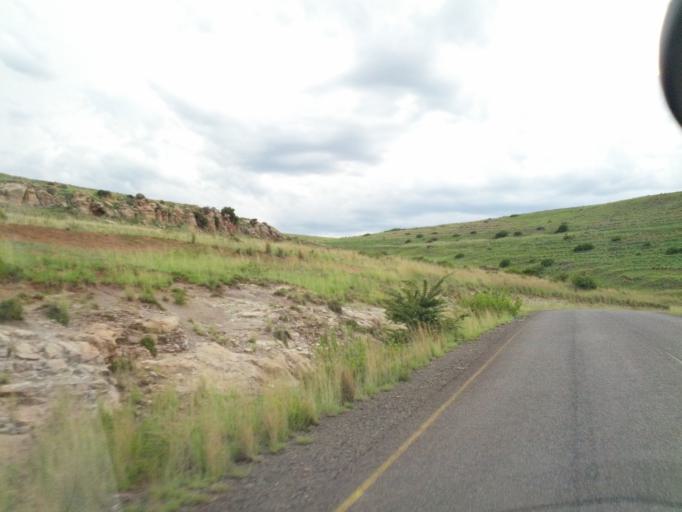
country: LS
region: Qacha's Nek
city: Qacha's Nek
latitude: -30.0533
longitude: 28.4995
